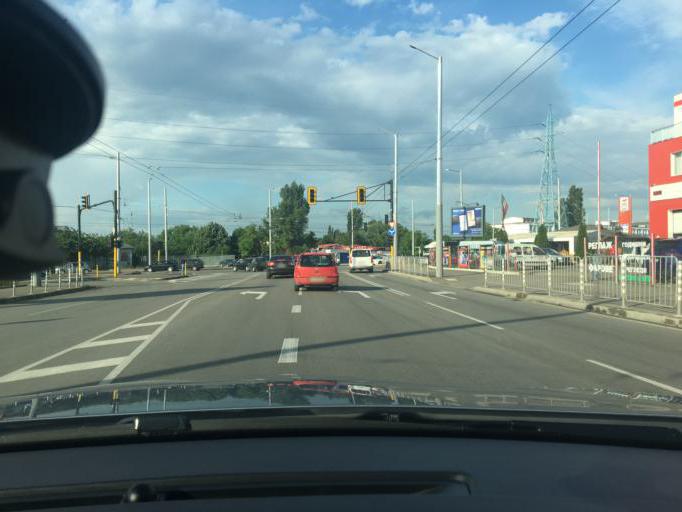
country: BG
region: Sofia-Capital
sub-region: Stolichna Obshtina
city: Sofia
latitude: 42.6745
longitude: 23.3755
